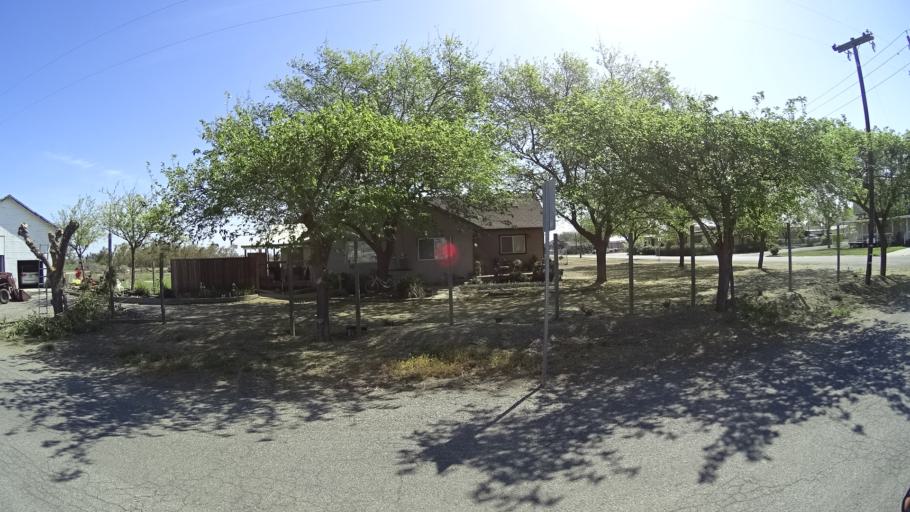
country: US
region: California
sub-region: Glenn County
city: Willows
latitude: 39.5317
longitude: -122.1887
